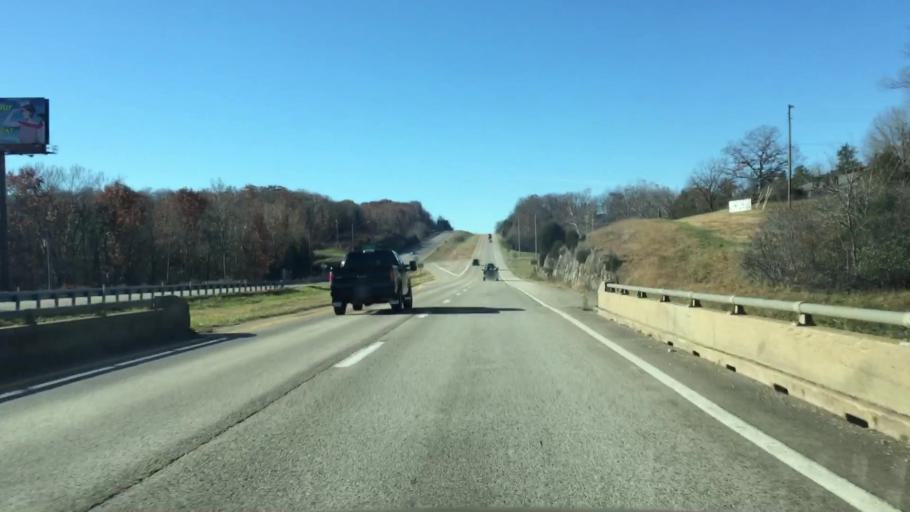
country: US
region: Missouri
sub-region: Cole County
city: Wardsville
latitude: 38.5195
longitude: -92.2332
